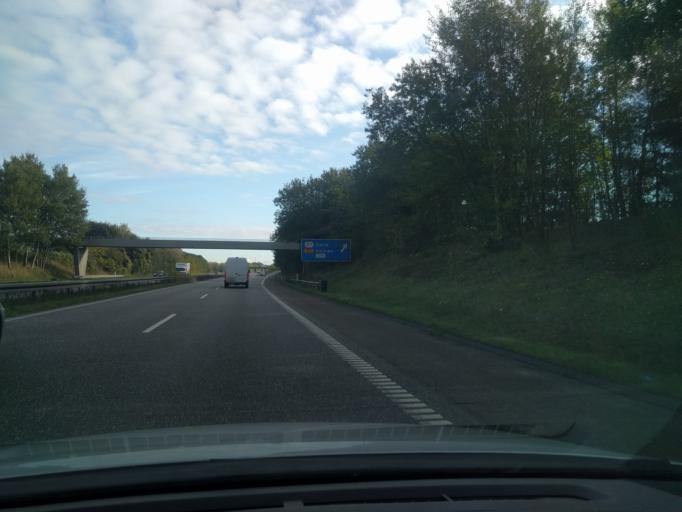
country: DK
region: Zealand
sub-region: Soro Kommune
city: Soro
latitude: 55.4489
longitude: 11.5555
